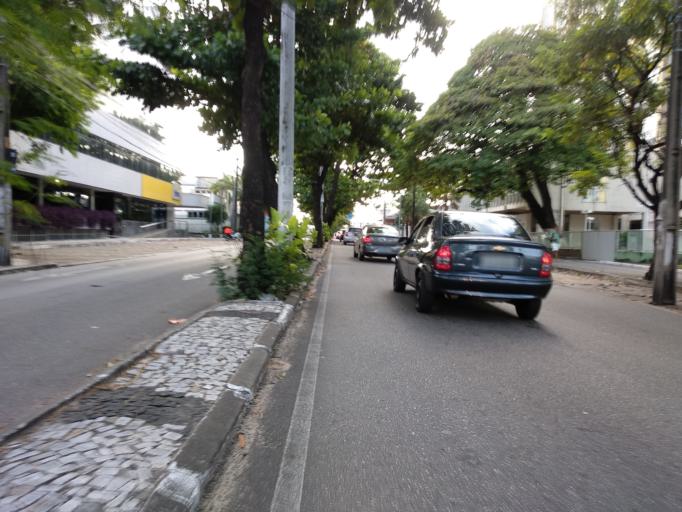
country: BR
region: Ceara
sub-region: Fortaleza
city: Fortaleza
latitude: -3.7289
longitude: -38.5387
